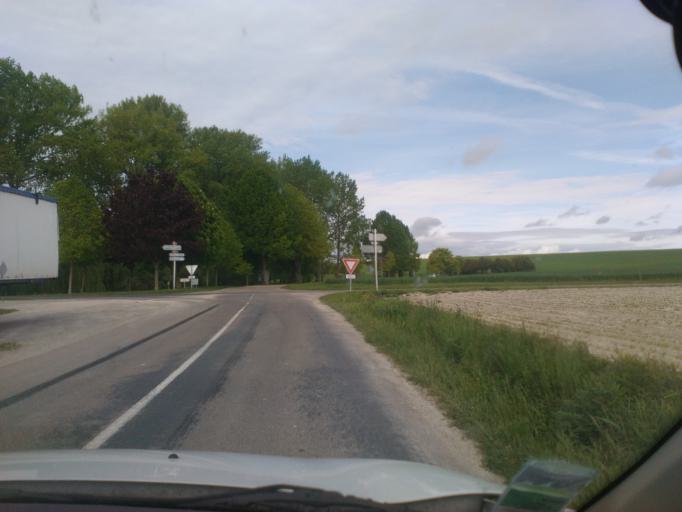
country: FR
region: Champagne-Ardenne
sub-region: Departement de l'Aube
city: Marigny-le-Chatel
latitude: 48.3620
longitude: 3.7113
